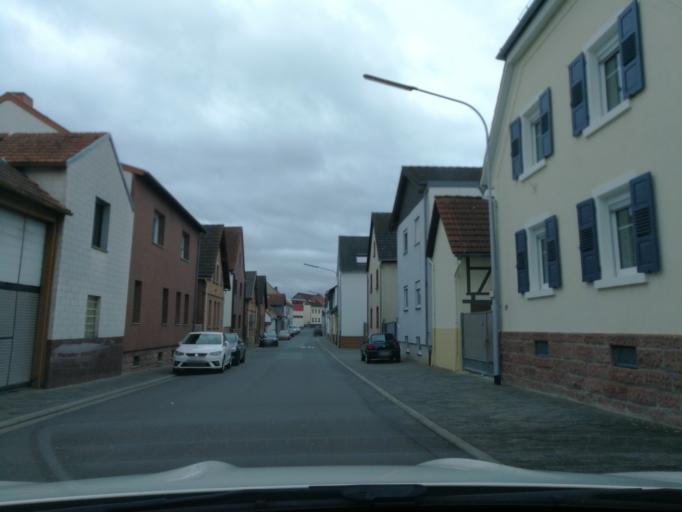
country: DE
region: Hesse
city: Reinheim
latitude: 49.8453
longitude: 8.8294
